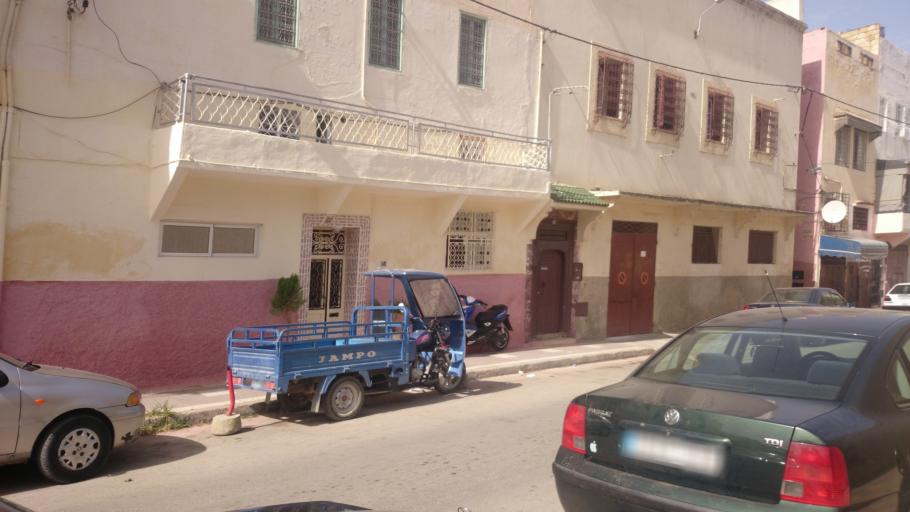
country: MA
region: Meknes-Tafilalet
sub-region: Meknes
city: Meknes
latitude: 33.8987
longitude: -5.5637
